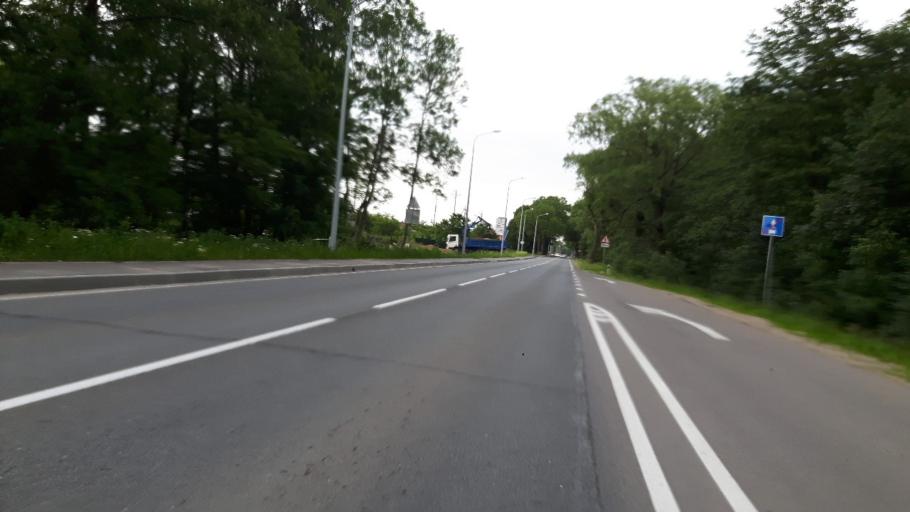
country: RU
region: Kaliningrad
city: Vzmorye
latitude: 54.6419
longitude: 20.3427
